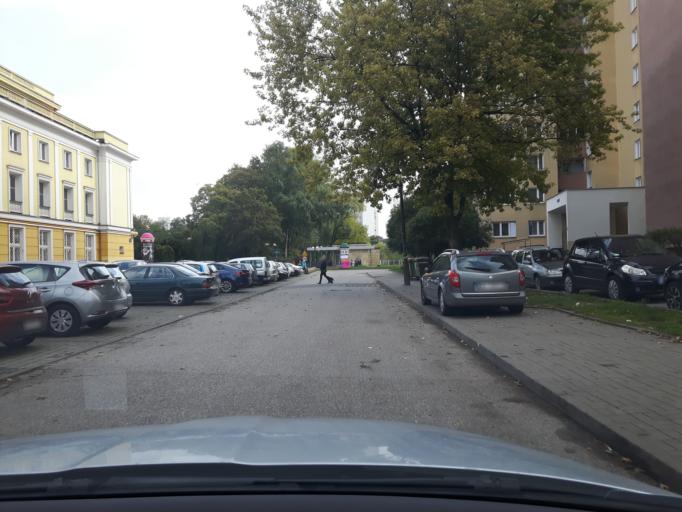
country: PL
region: Masovian Voivodeship
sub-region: Warszawa
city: Targowek
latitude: 52.2725
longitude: 21.0488
